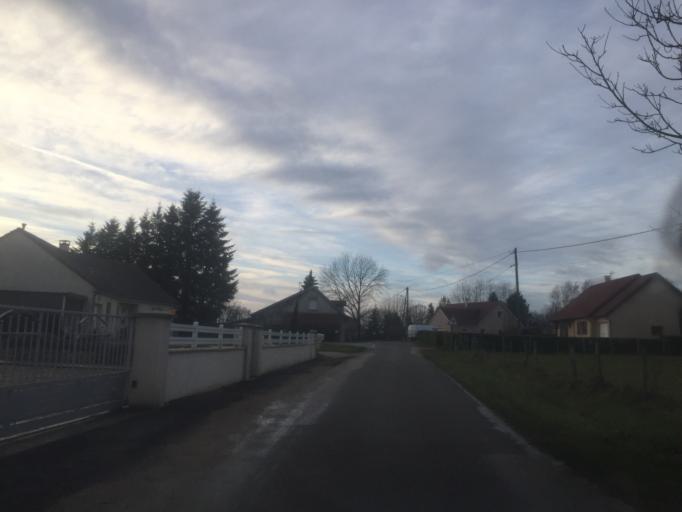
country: FR
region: Franche-Comte
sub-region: Departement du Jura
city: Orchamps
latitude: 47.1283
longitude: 5.6712
